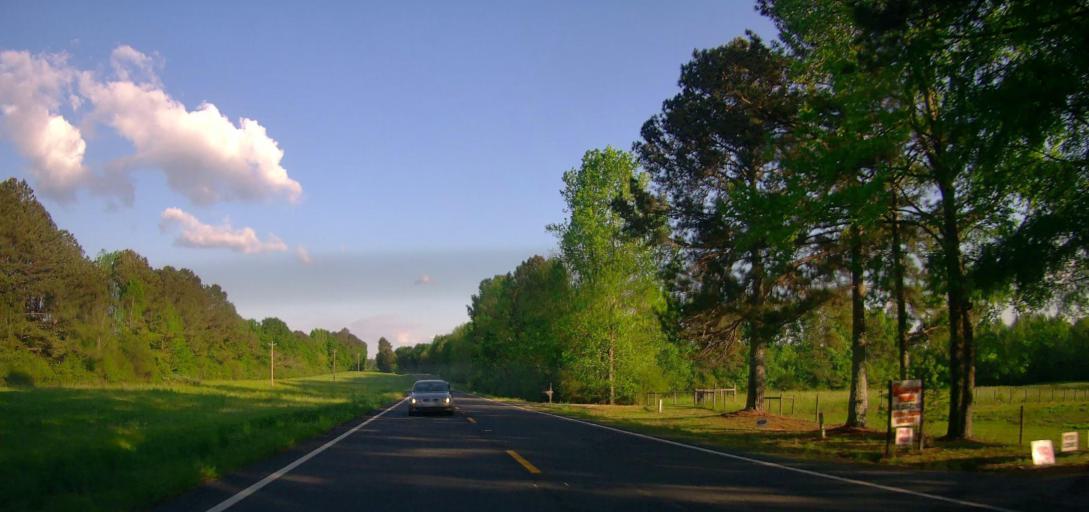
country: US
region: Georgia
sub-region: Jasper County
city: Monticello
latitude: 33.4118
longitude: -83.6054
